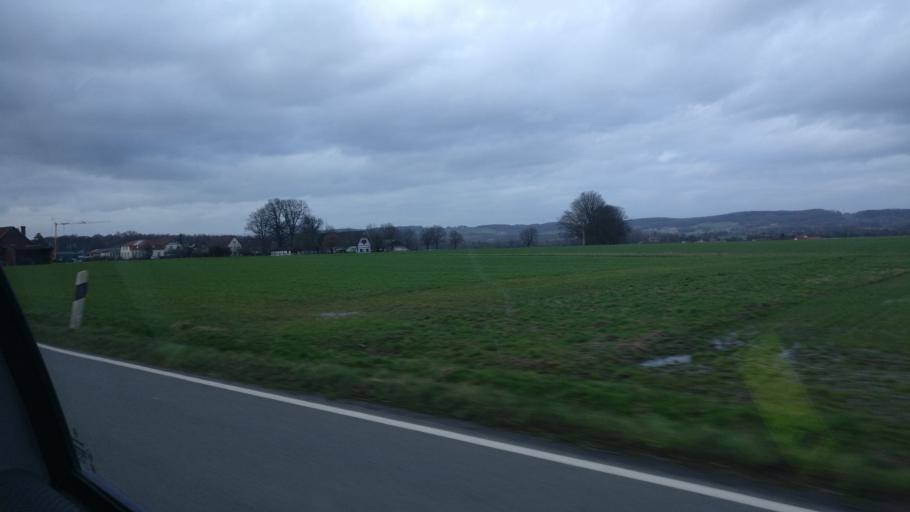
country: DE
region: North Rhine-Westphalia
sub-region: Regierungsbezirk Detmold
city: Lage
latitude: 52.0268
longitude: 8.7786
